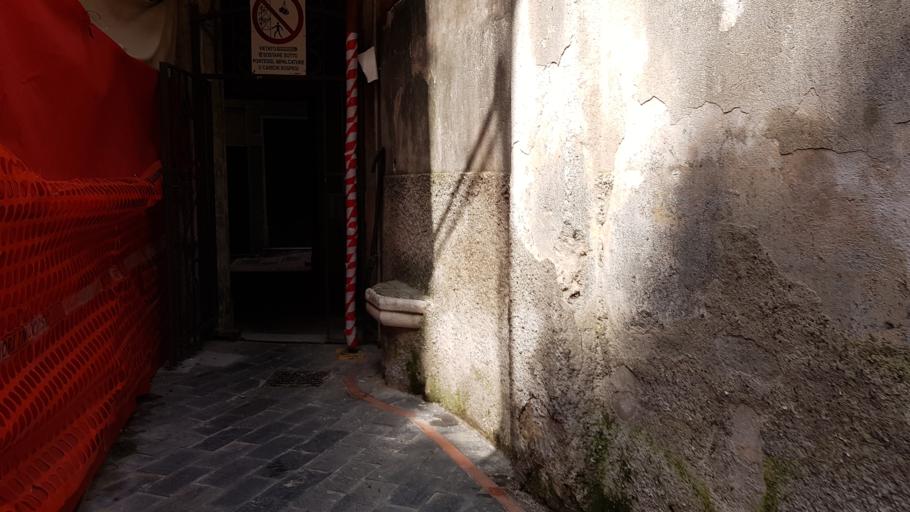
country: IT
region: Liguria
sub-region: Provincia di Genova
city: Genoa
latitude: 44.4127
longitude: 8.9356
